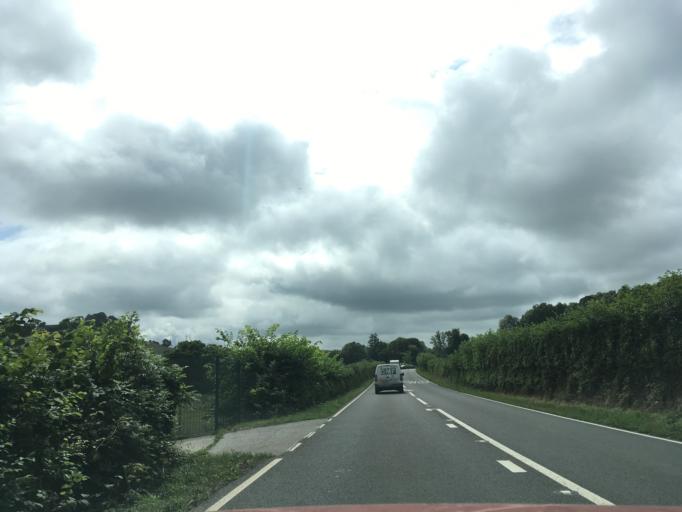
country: GB
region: Wales
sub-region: Carmarthenshire
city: Llangathen
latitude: 51.8840
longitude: -4.0670
